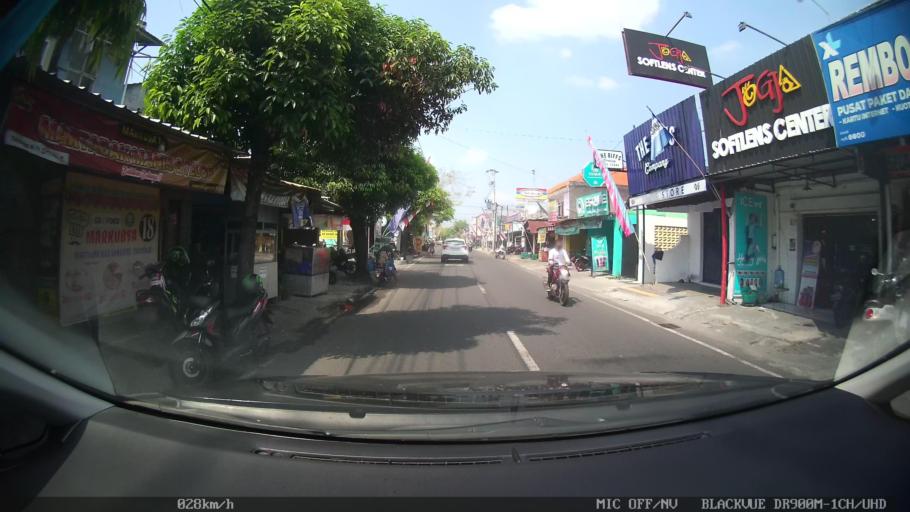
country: ID
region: Daerah Istimewa Yogyakarta
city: Yogyakarta
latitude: -7.8076
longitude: 110.3879
